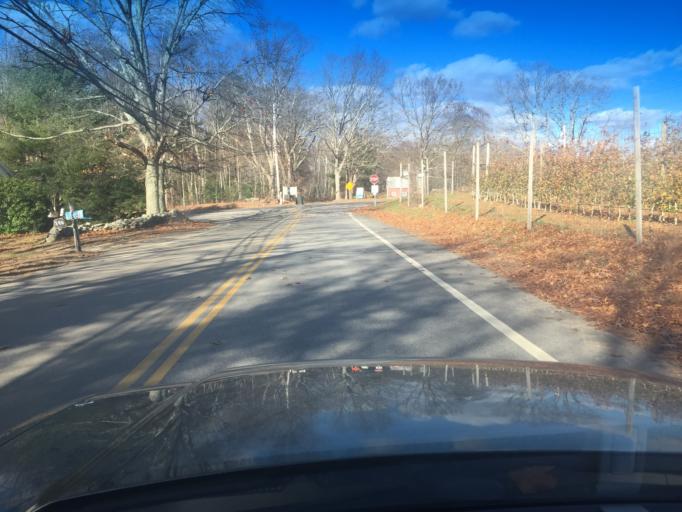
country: US
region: Rhode Island
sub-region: Providence County
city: North Scituate
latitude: 41.8567
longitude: -71.5913
